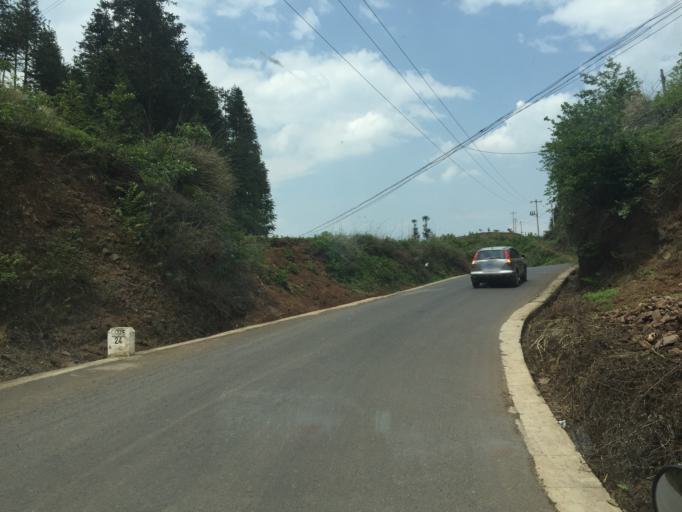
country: CN
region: Guangxi Zhuangzu Zizhiqu
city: Xinzhou
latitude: 25.6988
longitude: 105.2294
